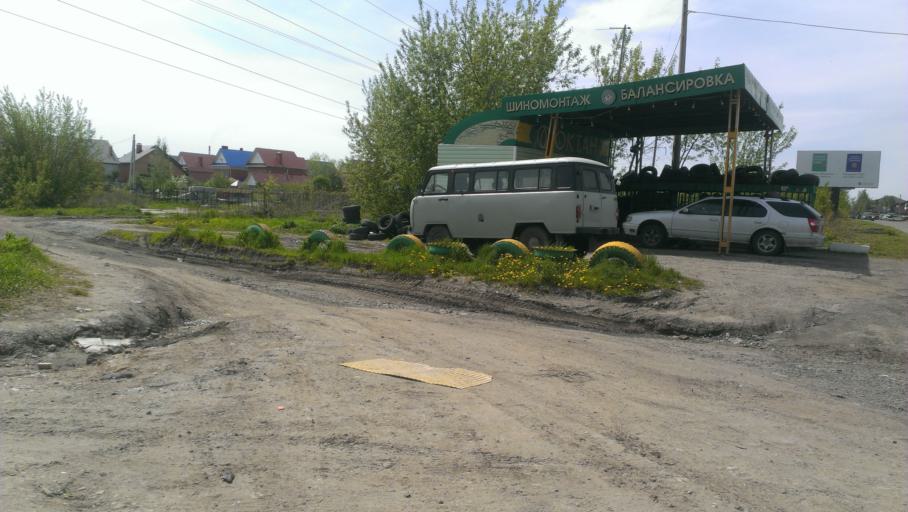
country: RU
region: Altai Krai
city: Novosilikatnyy
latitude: 53.3570
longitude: 83.6588
